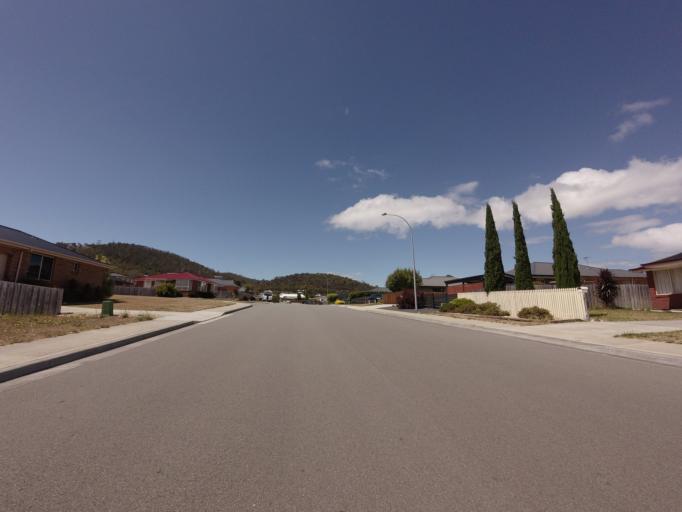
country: AU
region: Tasmania
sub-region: Clarence
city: Rokeby
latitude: -42.8993
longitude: 147.4529
